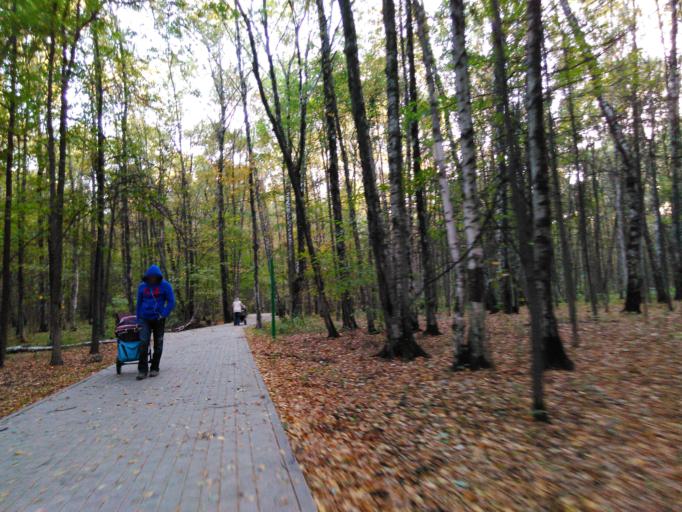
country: RU
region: Moscow
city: Troparevo
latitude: 55.6559
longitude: 37.5081
